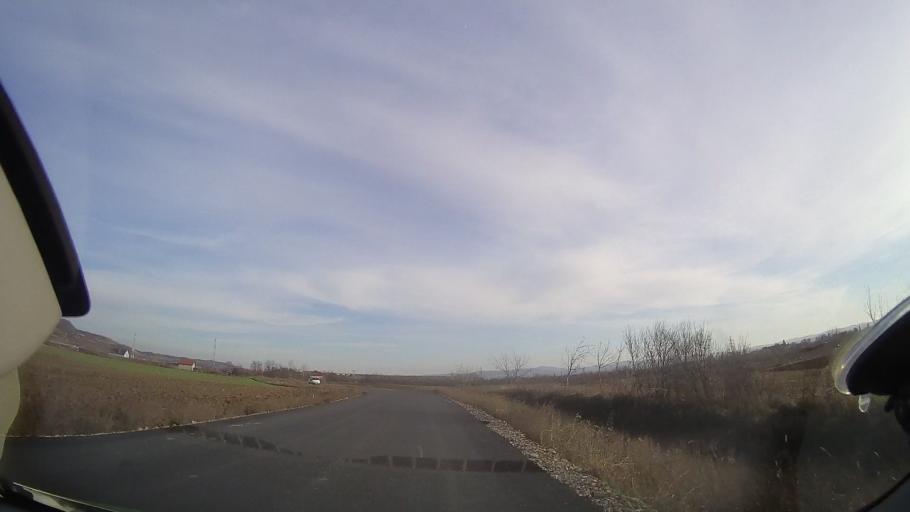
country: RO
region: Bihor
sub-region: Comuna Tileagd
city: Tileagd
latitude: 47.0826
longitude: 22.1914
